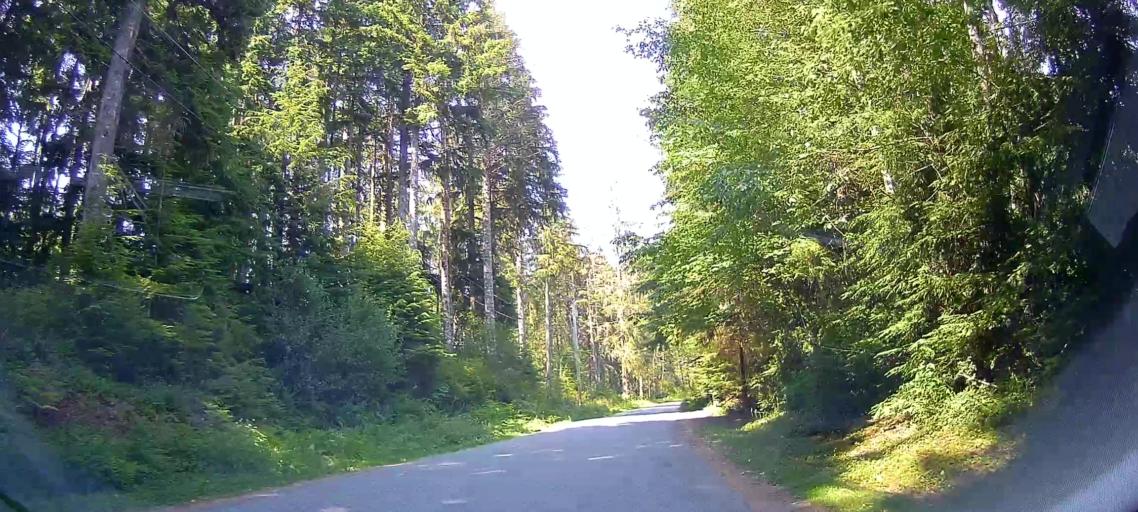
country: US
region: Washington
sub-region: Snohomish County
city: Arlington Heights
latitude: 48.3237
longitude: -122.0388
